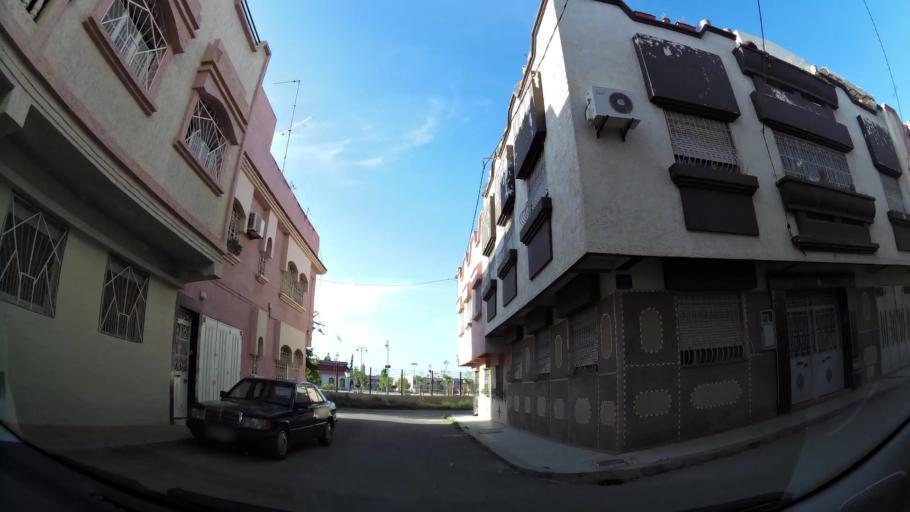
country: MA
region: Oriental
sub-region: Oujda-Angad
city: Oujda
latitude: 34.6967
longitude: -1.9123
